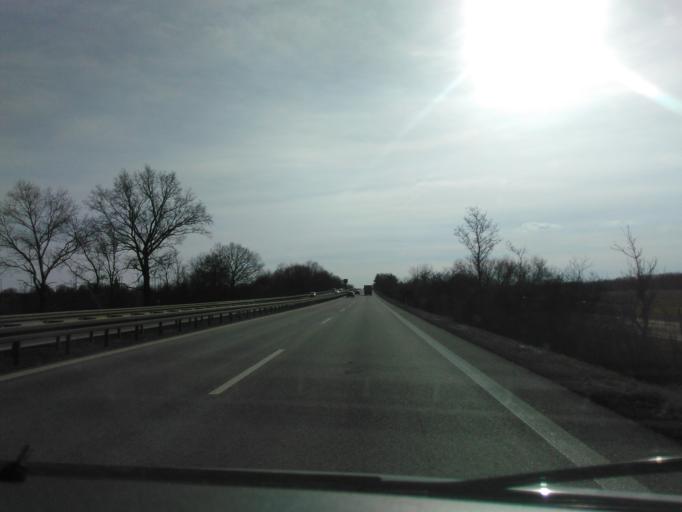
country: DE
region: Brandenburg
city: Calau
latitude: 51.7797
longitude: 13.8728
